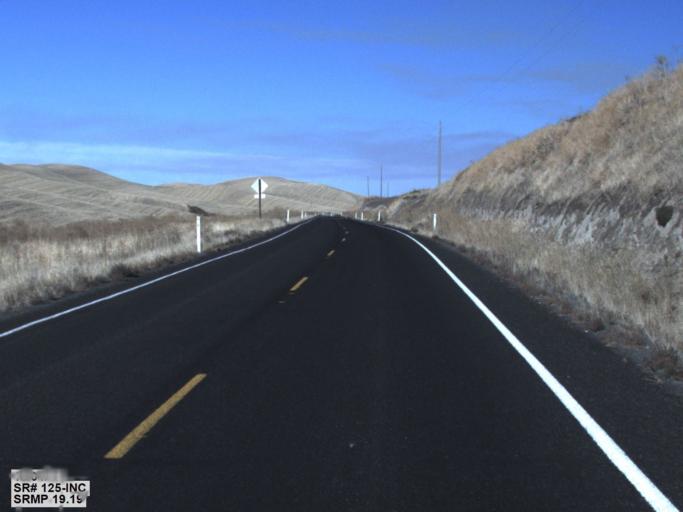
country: US
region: Washington
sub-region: Walla Walla County
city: Walla Walla
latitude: 46.2382
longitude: -118.3689
